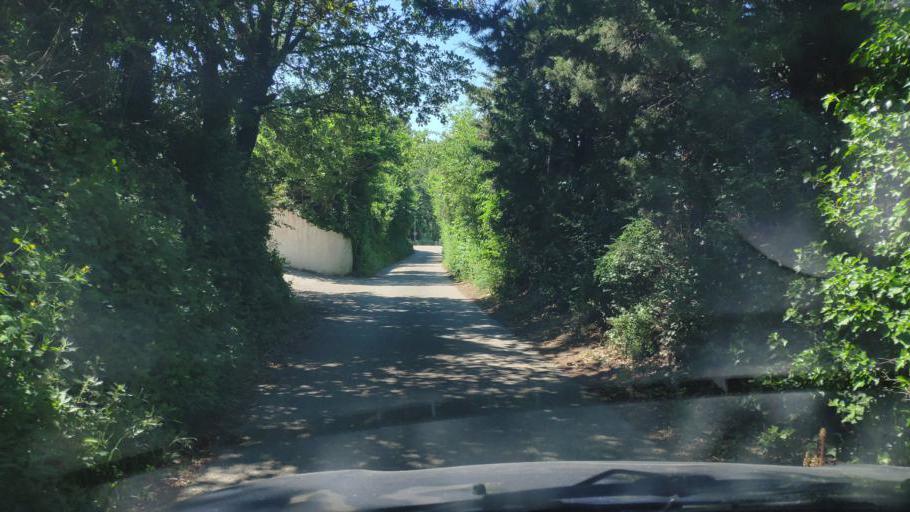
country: FR
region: Provence-Alpes-Cote d'Azur
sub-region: Departement du Vaucluse
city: Loriol-du-Comtat
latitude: 44.0732
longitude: 5.0153
